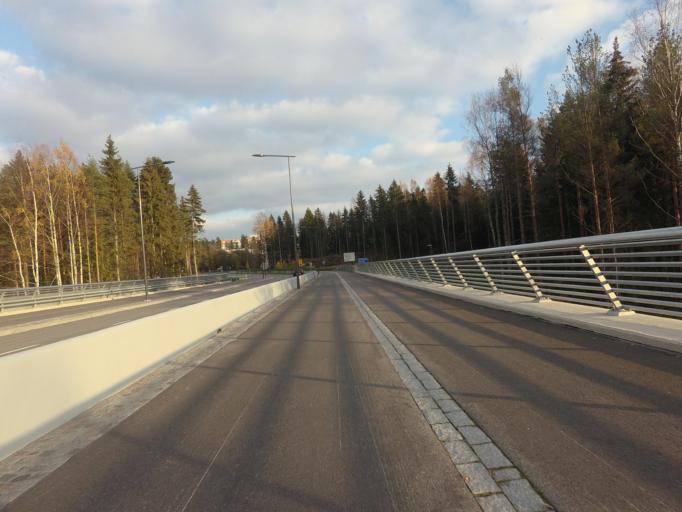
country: FI
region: Uusimaa
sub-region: Helsinki
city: Koukkuniemi
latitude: 60.1564
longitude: 24.7227
